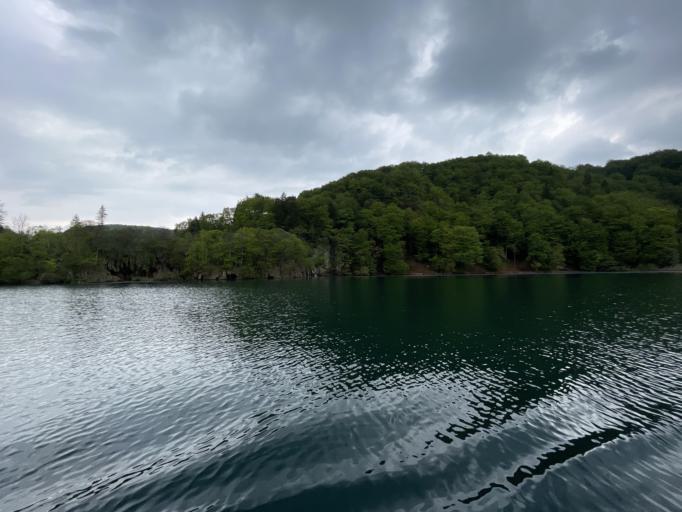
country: HR
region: Licko-Senjska
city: Jezerce
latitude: 44.8814
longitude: 15.6143
